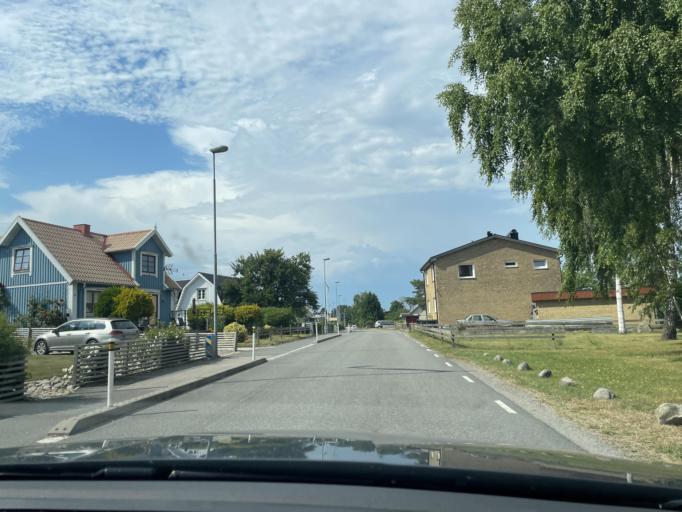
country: SE
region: Blekinge
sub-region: Karlshamns Kommun
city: Morrum
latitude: 56.0471
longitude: 14.7573
